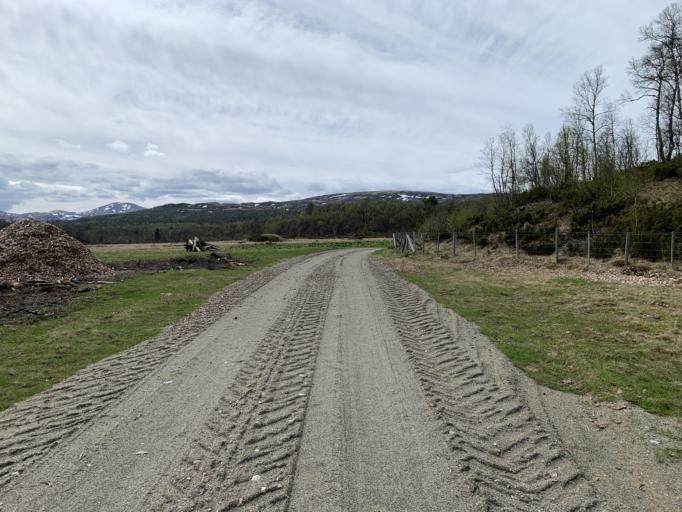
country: NO
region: Hedmark
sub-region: Alvdal
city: Alvdal
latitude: 62.4124
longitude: 10.4024
